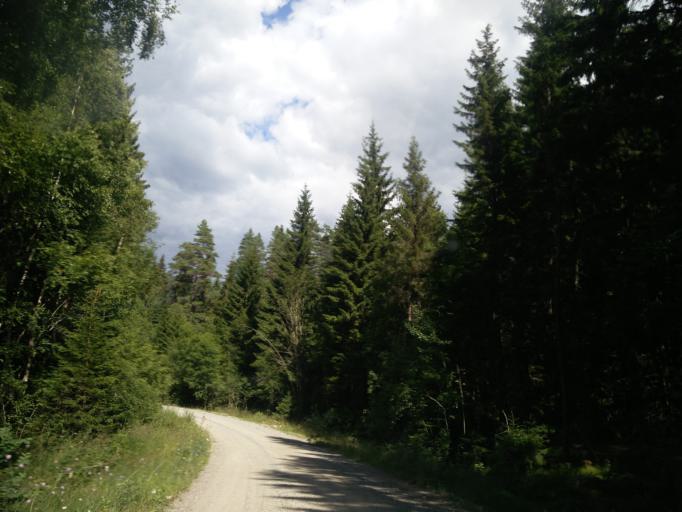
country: SE
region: OErebro
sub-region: Ljusnarsbergs Kommun
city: Kopparberg
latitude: 59.7865
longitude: 14.7802
